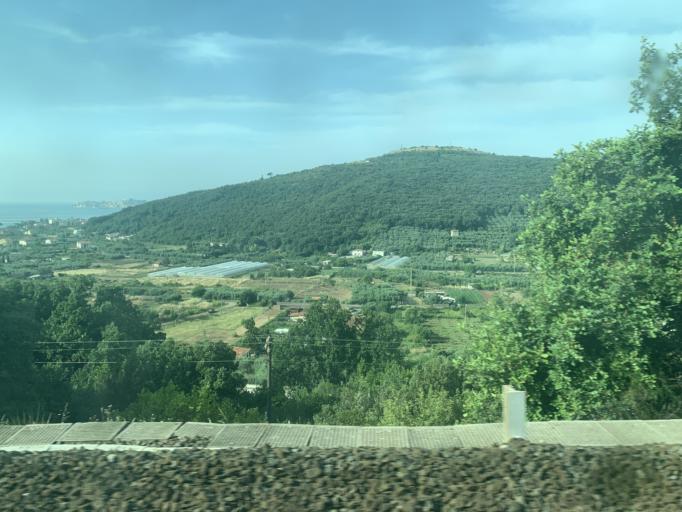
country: IT
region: Latium
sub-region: Provincia di Latina
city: Gaeta
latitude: 41.2556
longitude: 13.5727
